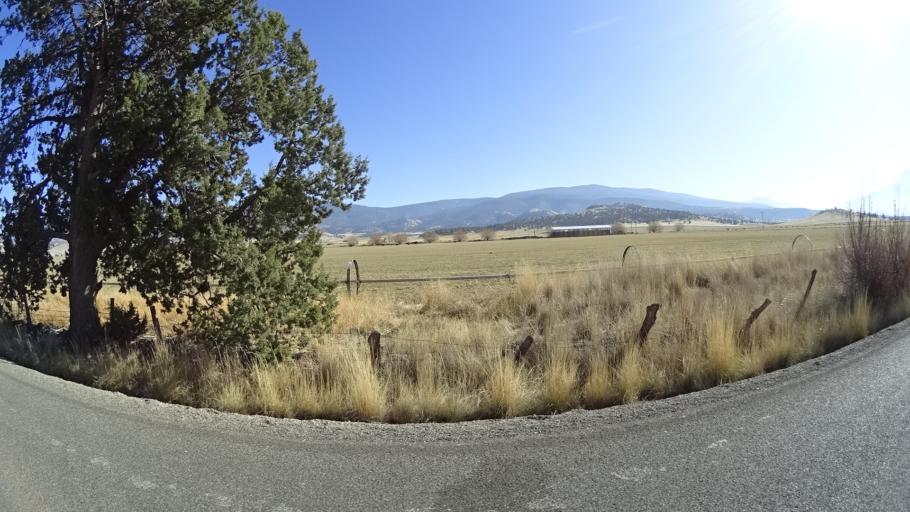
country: US
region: California
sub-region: Siskiyou County
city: Montague
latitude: 41.6810
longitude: -122.3698
